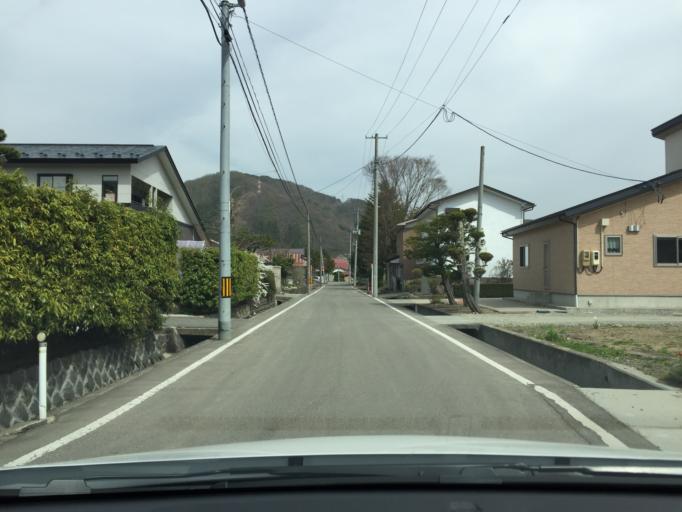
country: JP
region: Fukushima
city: Inawashiro
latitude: 37.5167
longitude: 140.1336
